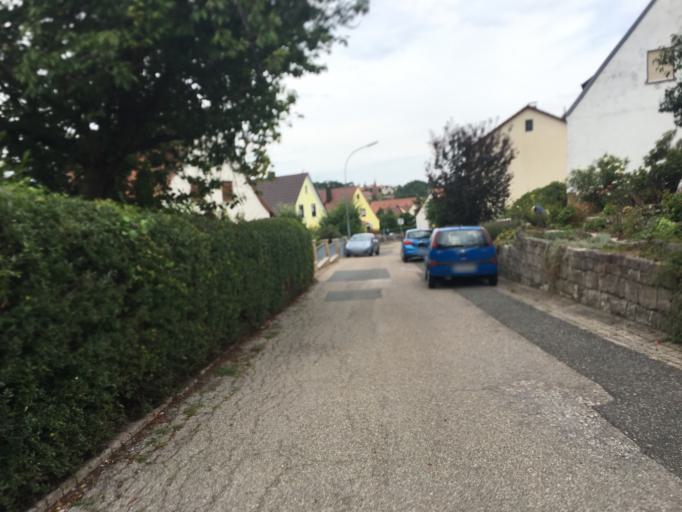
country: DE
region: Bavaria
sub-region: Regierungsbezirk Mittelfranken
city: Wilhermsdorf
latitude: 49.4826
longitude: 10.7084
